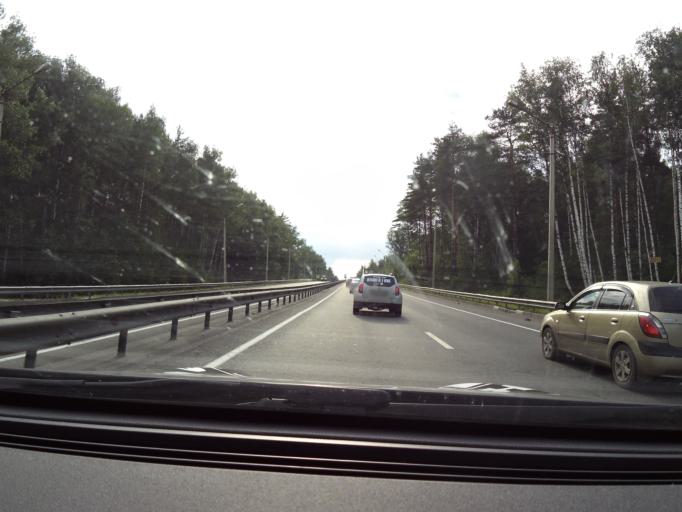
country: RU
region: Vladimir
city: Novovyazniki
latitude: 56.2200
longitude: 42.1732
